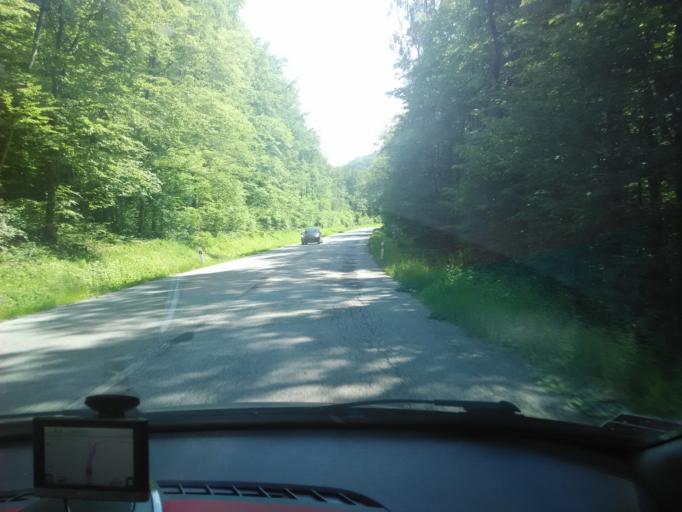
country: SK
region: Banskobystricky
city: Revuca
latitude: 48.6312
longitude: 20.2884
